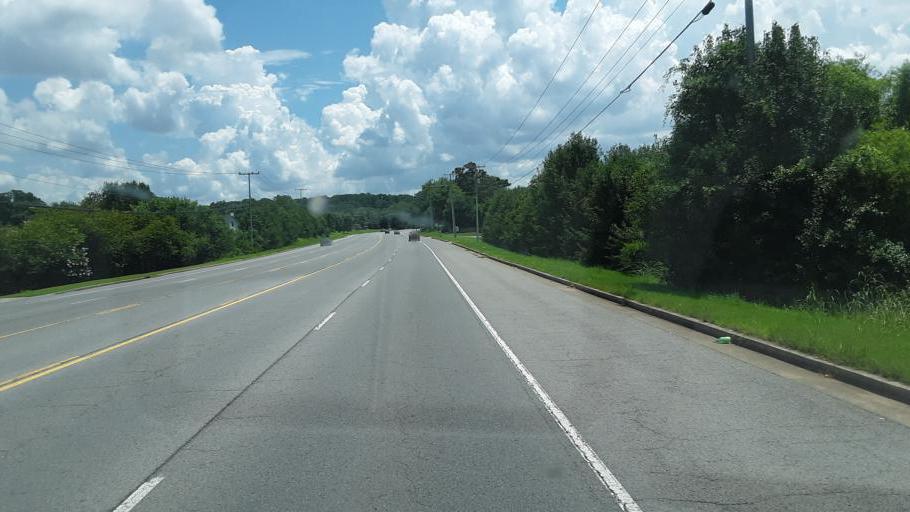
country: US
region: Kentucky
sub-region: Christian County
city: Oak Grove
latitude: 36.6303
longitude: -87.3798
